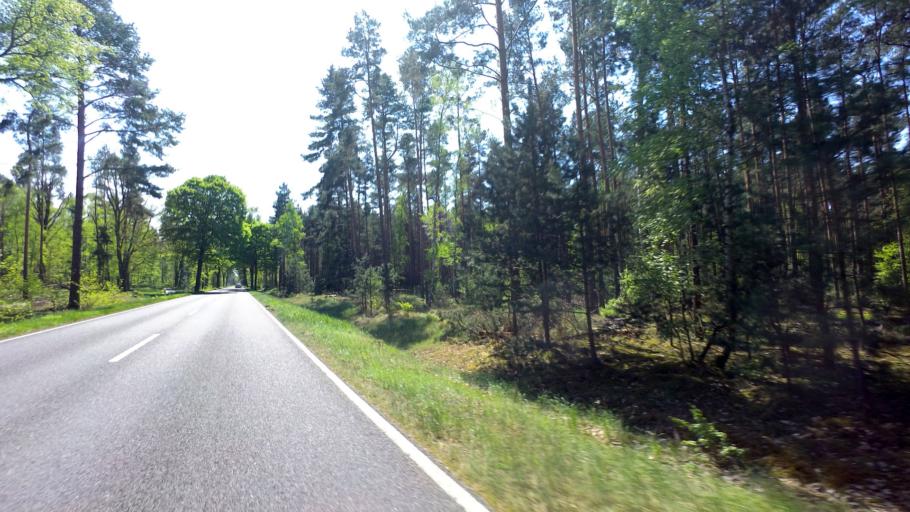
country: DE
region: Brandenburg
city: Halbe
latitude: 52.1483
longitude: 13.7458
